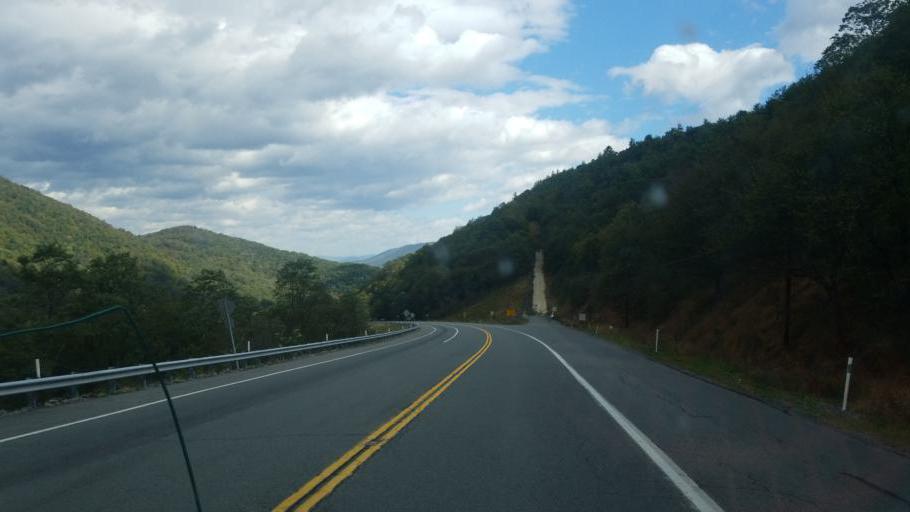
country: US
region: Pennsylvania
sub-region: Fulton County
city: McConnellsburg
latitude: 39.9299
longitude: -77.9336
